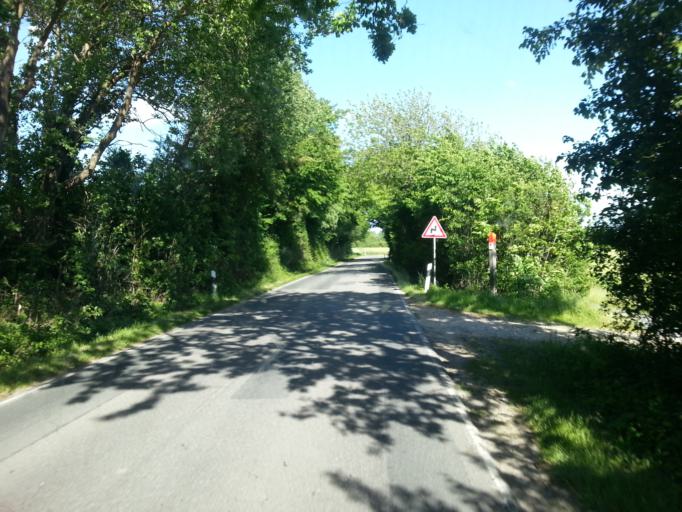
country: DE
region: Schleswig-Holstein
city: Ratekau
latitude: 53.9897
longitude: 10.7269
